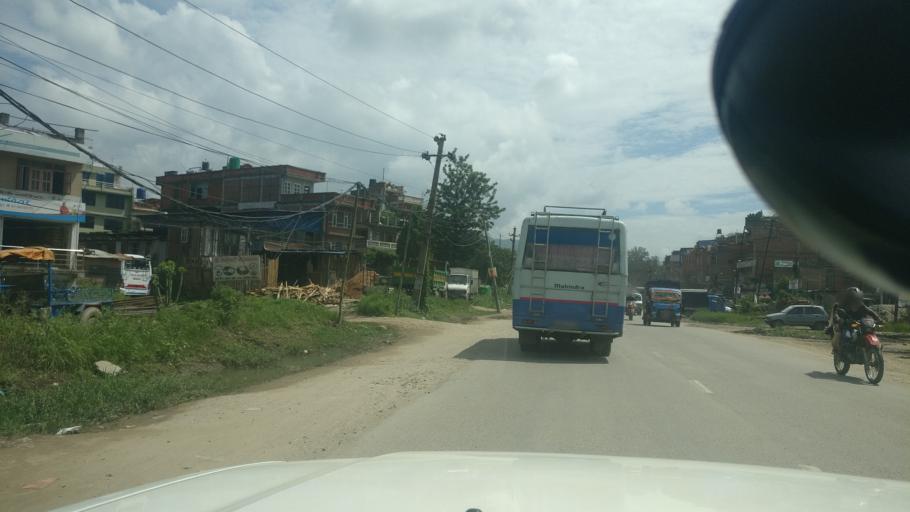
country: NP
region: Central Region
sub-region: Bagmati Zone
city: Bhaktapur
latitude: 27.6665
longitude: 85.4350
